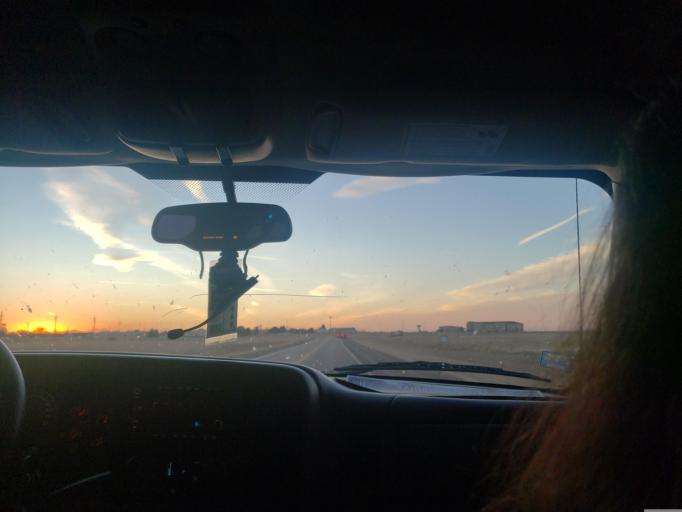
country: US
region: Kansas
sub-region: Seward County
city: Liberal
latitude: 37.0705
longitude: -100.9136
